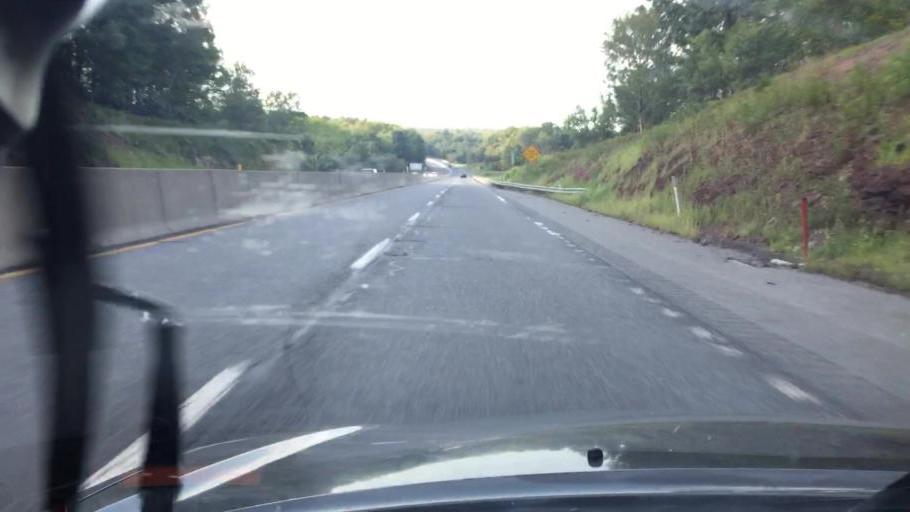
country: US
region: Pennsylvania
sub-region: Carbon County
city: Towamensing Trails
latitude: 41.0030
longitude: -75.6347
